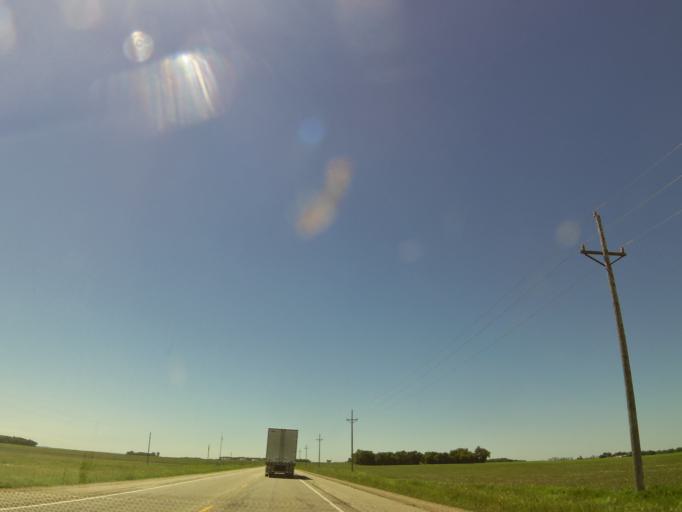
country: US
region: Minnesota
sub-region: Mahnomen County
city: Mahnomen
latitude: 47.2756
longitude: -95.9334
